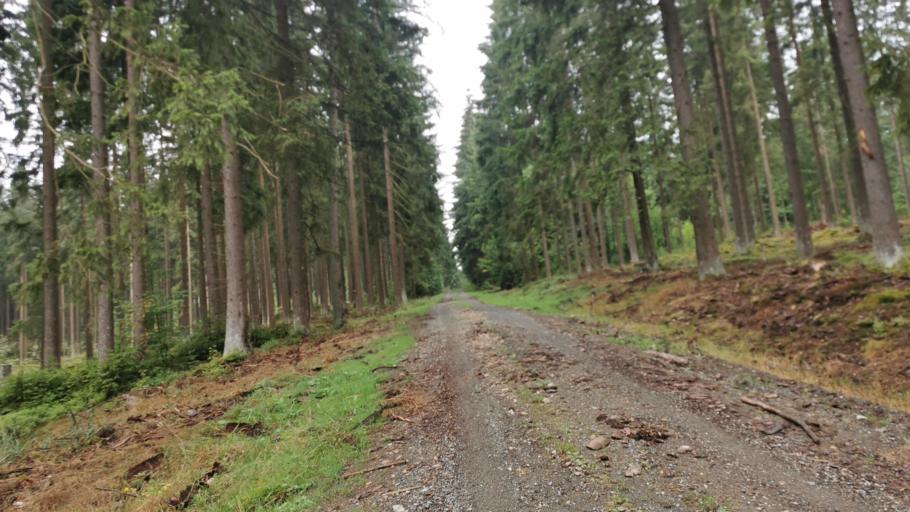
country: DE
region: Thuringia
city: Wurzbach
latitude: 50.4412
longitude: 11.5258
